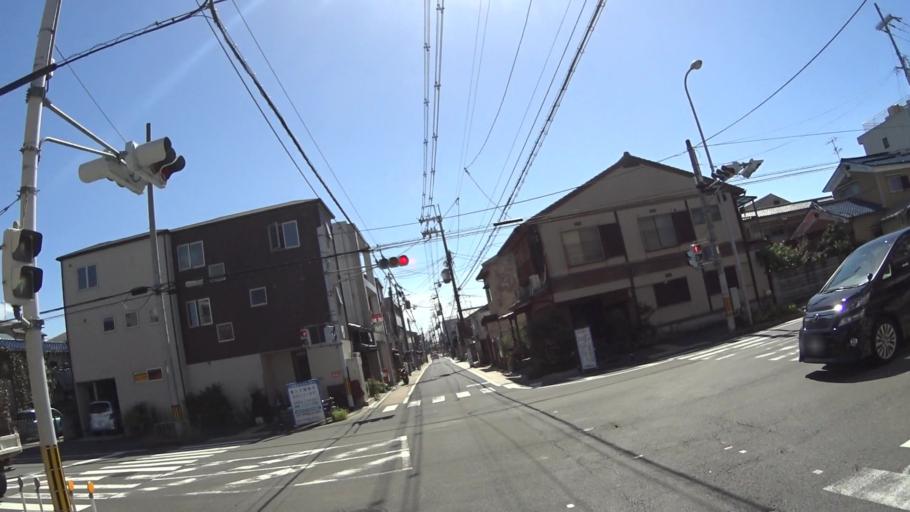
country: JP
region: Kyoto
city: Muko
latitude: 34.9452
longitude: 135.7583
